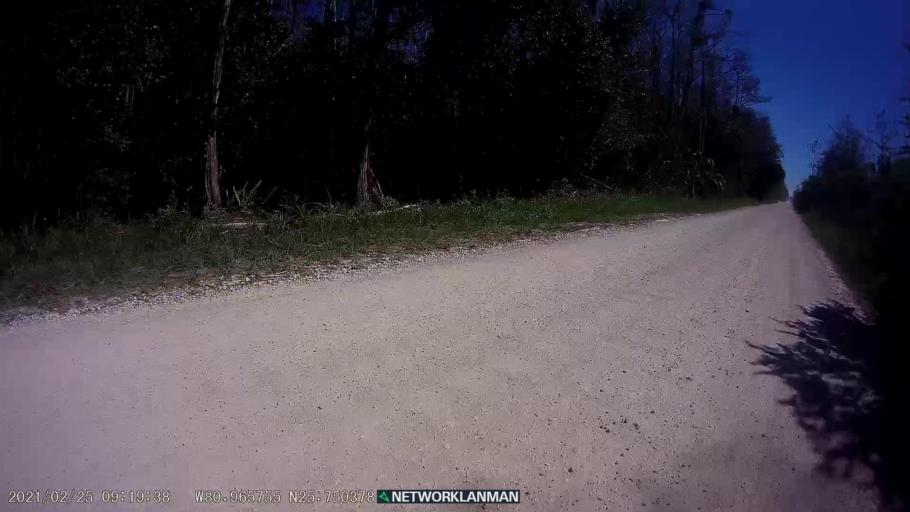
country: US
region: Florida
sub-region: Miami-Dade County
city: The Hammocks
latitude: 25.7503
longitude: -80.9656
